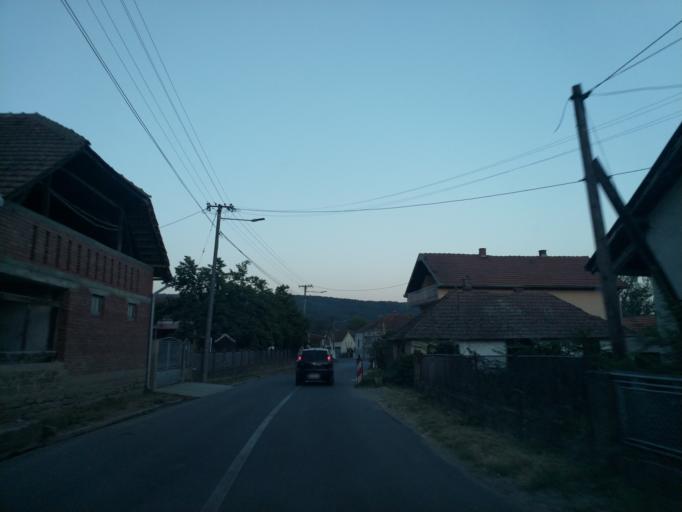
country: RS
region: Central Serbia
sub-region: Rasinski Okrug
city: Krusevac
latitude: 43.6241
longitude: 21.3596
